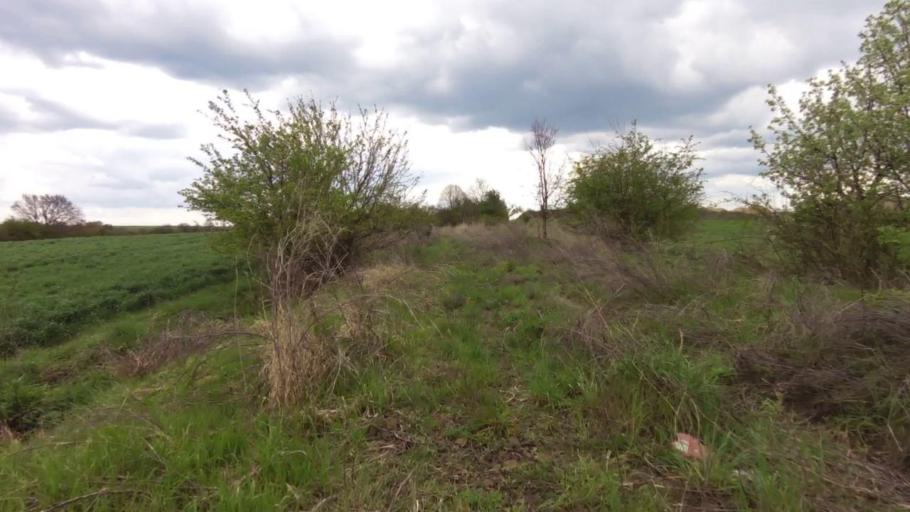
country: PL
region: West Pomeranian Voivodeship
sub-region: Powiat choszczenski
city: Pelczyce
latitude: 53.0427
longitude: 15.2929
